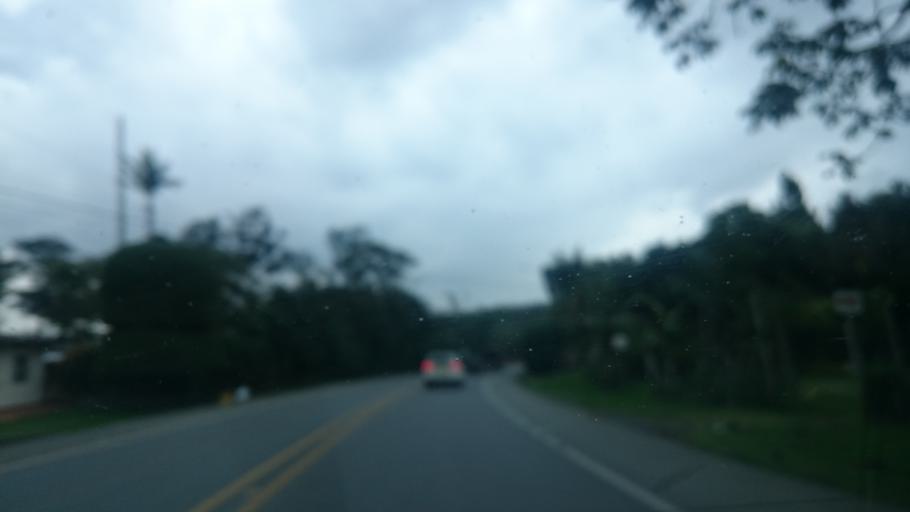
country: CO
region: Cauca
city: Cajibio
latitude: 2.5218
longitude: -76.5484
